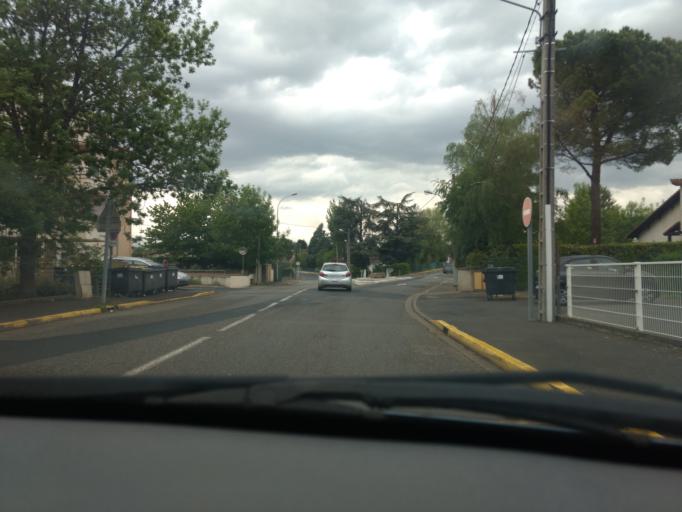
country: FR
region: Auvergne
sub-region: Departement du Puy-de-Dome
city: Pont-du-Chateau
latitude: 45.8008
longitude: 3.2427
